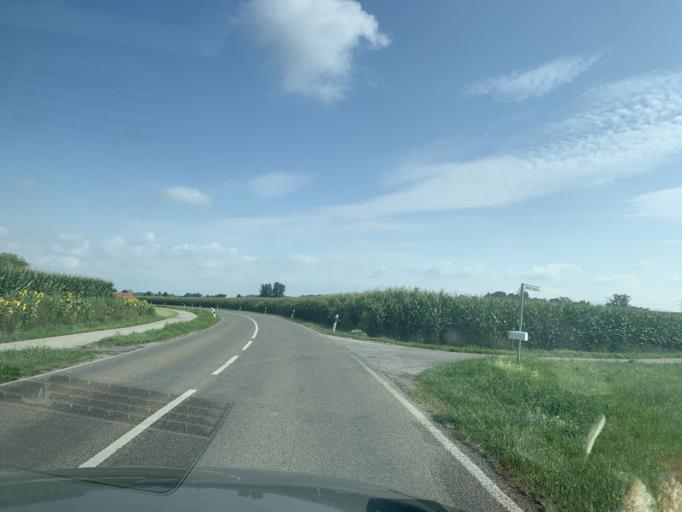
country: DE
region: Bavaria
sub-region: Swabia
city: Kissing
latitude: 48.2887
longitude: 10.9817
